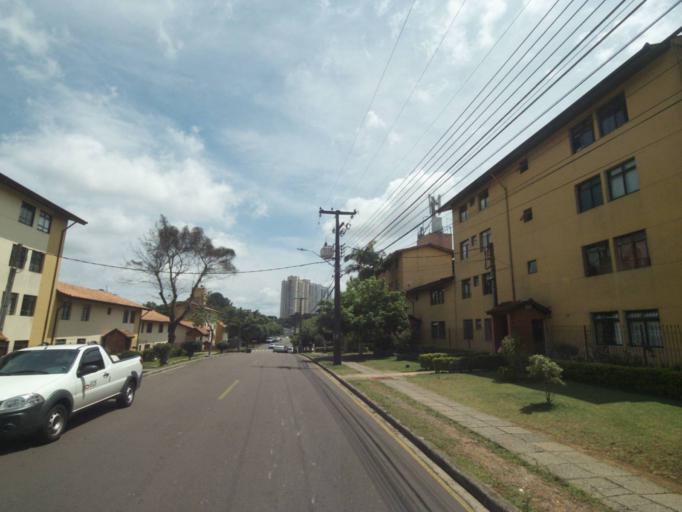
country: BR
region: Parana
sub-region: Curitiba
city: Curitiba
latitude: -25.4514
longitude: -49.3539
